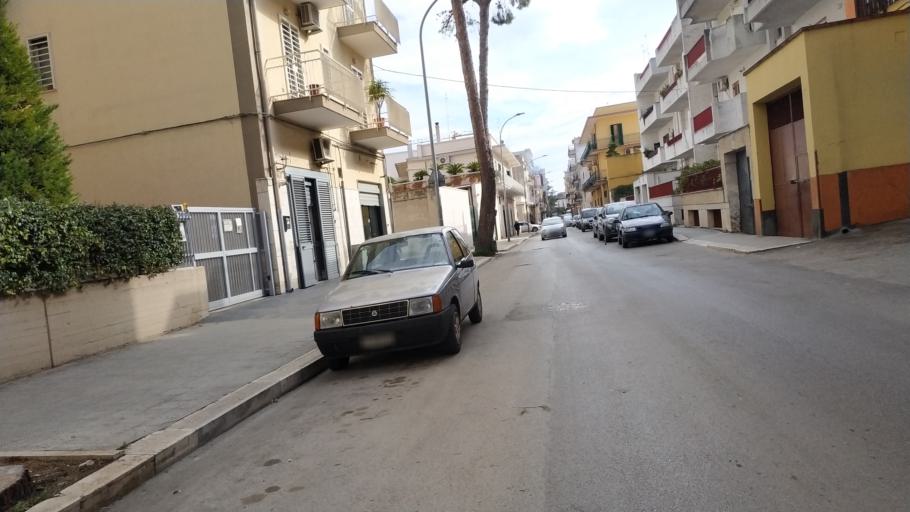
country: IT
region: Apulia
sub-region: Provincia di Bari
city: Bitonto
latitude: 41.1074
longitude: 16.6826
